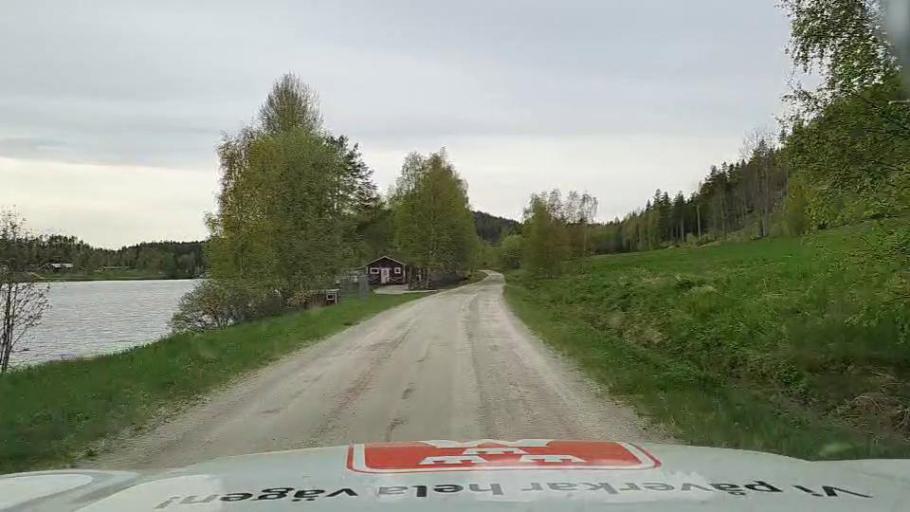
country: SE
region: Jaemtland
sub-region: Bergs Kommun
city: Hoverberg
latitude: 62.6864
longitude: 14.7869
